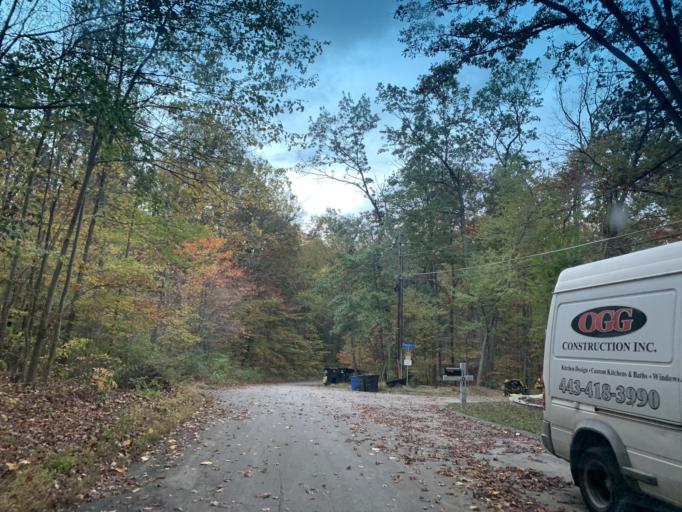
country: US
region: Maryland
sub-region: Harford County
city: South Bel Air
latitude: 39.5709
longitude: -76.3244
